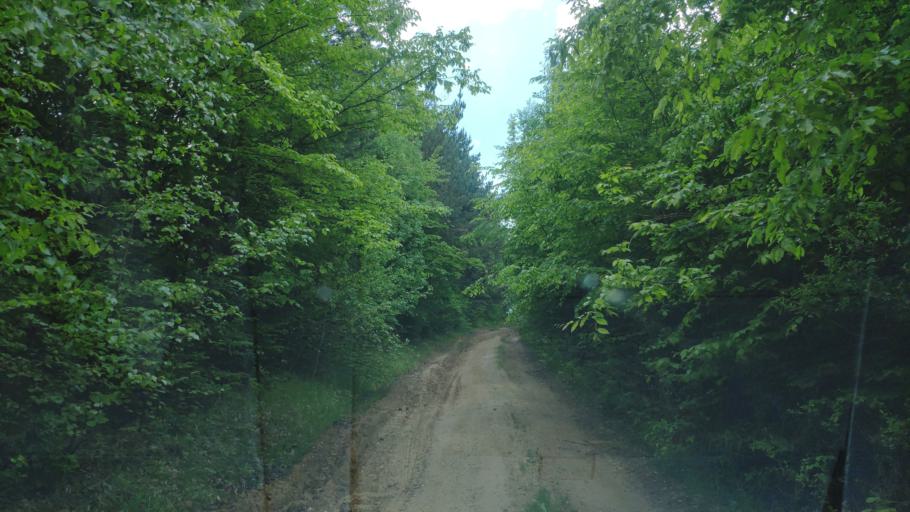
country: SK
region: Presovsky
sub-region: Okres Presov
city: Presov
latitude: 48.9399
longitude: 21.1193
